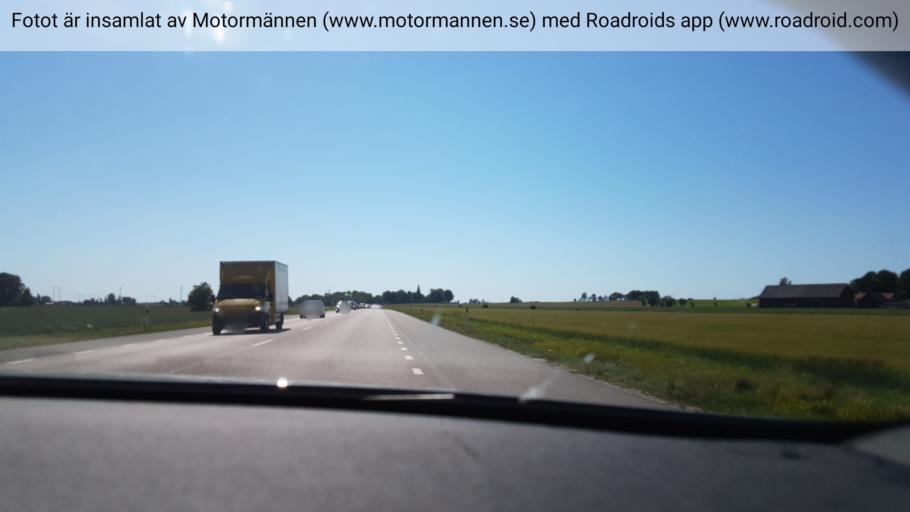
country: SE
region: Vaestra Goetaland
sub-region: Gotene Kommun
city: Goetene
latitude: 58.5140
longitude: 13.4230
